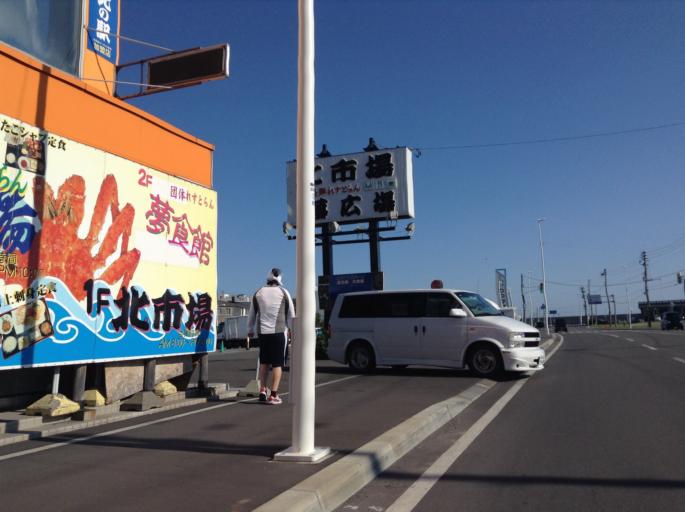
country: JP
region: Hokkaido
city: Wakkanai
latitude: 45.4169
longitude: 141.6780
